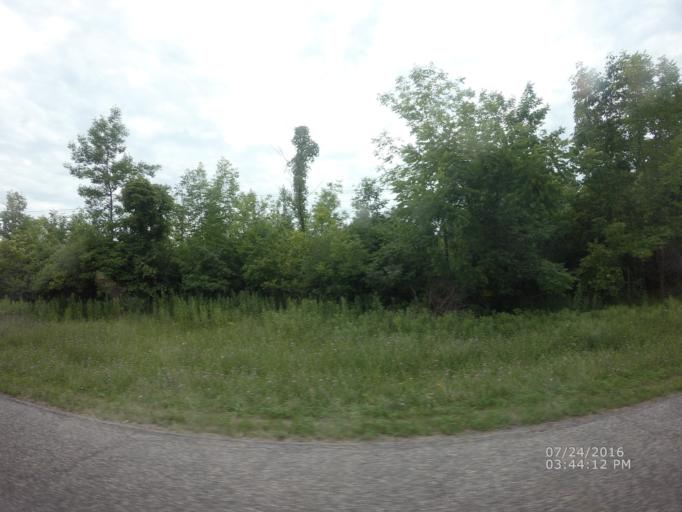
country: US
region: New York
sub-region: Onondaga County
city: Camillus
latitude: 43.0218
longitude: -76.3046
